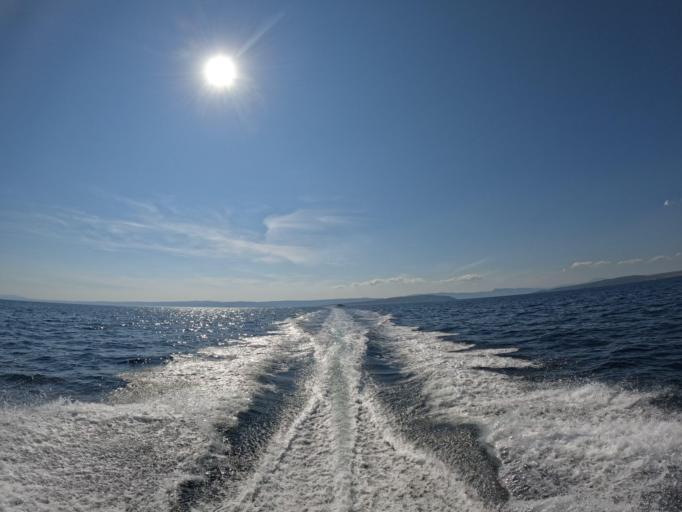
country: HR
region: Primorsko-Goranska
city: Punat
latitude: 44.9572
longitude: 14.6228
